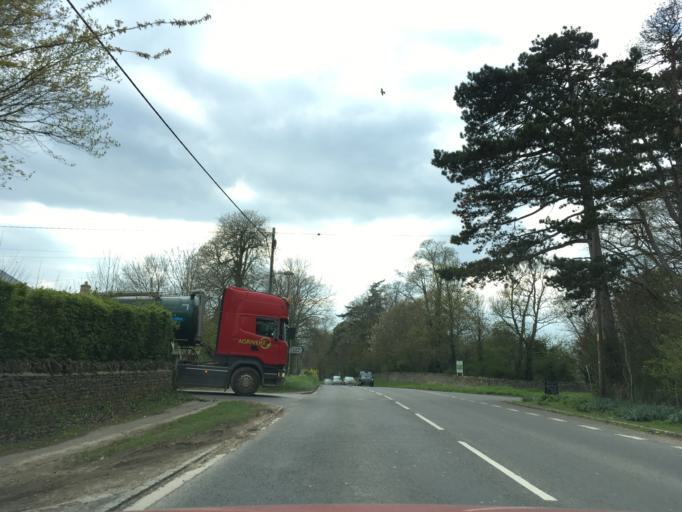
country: GB
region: England
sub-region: Oxfordshire
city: Woodstock
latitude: 51.8370
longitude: -1.3402
